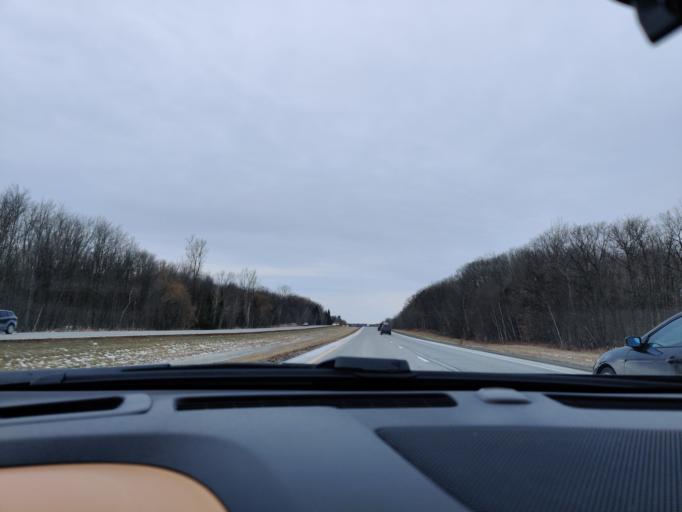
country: CA
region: Ontario
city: Prescott
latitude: 44.7903
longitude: -75.4382
